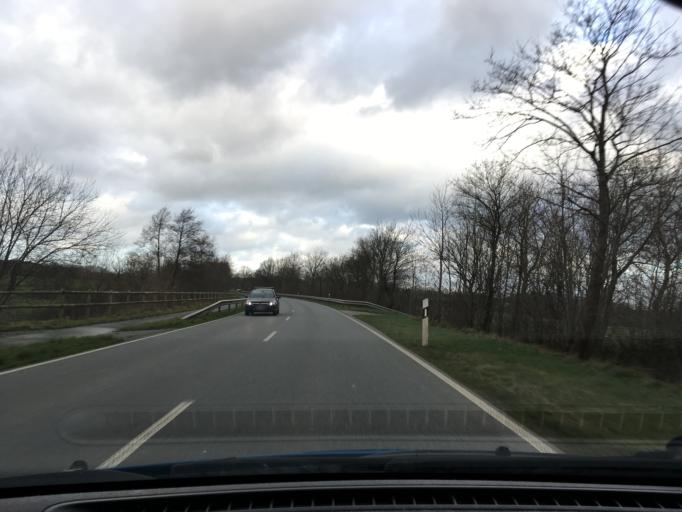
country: DE
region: Schleswig-Holstein
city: Kaisborstel
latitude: 54.0150
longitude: 9.4809
